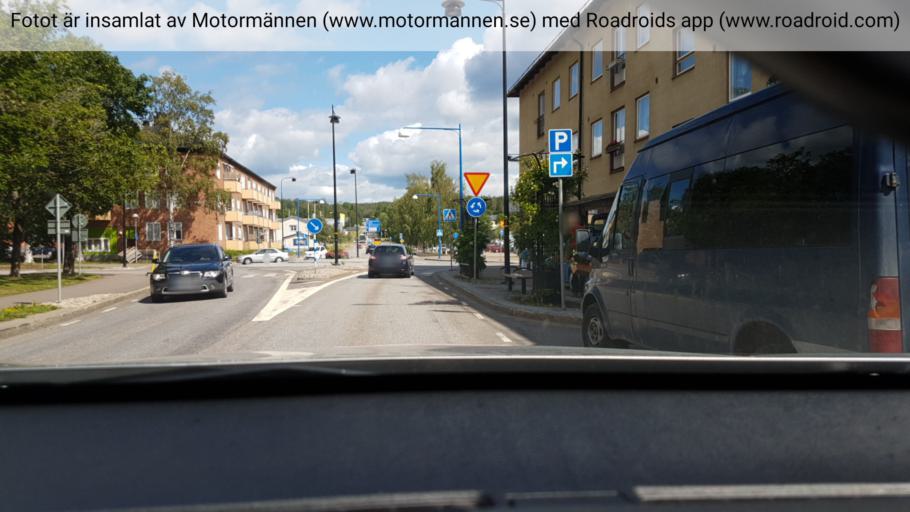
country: SE
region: Vaermland
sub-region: Filipstads Kommun
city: Filipstad
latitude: 59.7136
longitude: 14.1686
